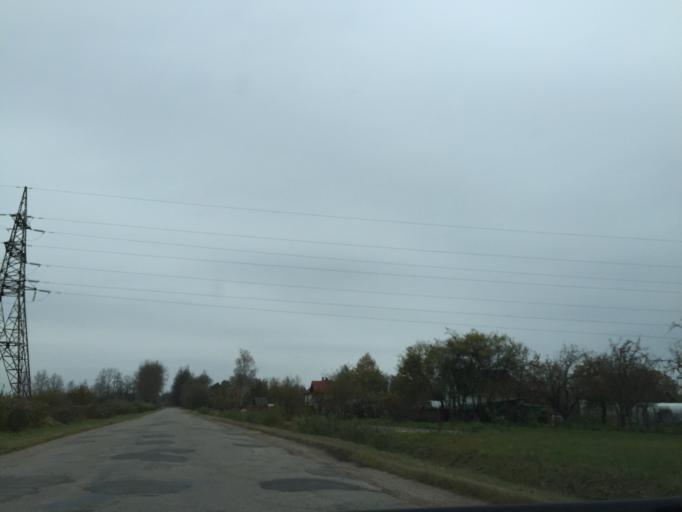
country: LV
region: Jelgava
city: Jelgava
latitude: 56.6329
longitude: 23.7462
